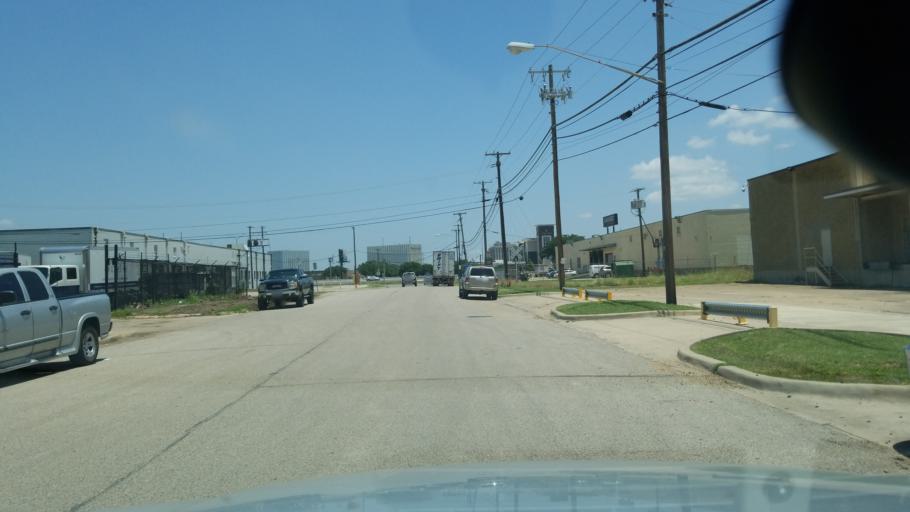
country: US
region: Texas
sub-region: Dallas County
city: Irving
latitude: 32.8206
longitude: -96.8797
